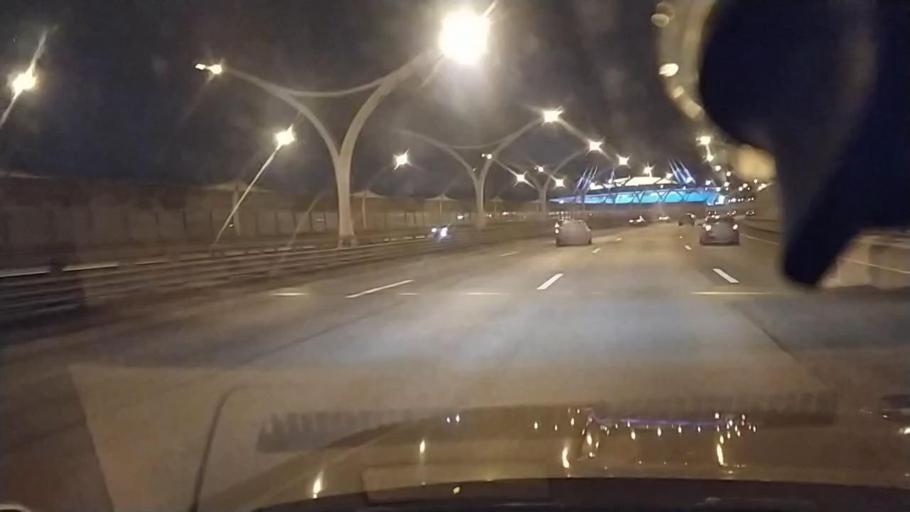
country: RU
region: St.-Petersburg
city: Staraya Derevnya
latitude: 59.9833
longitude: 30.2289
